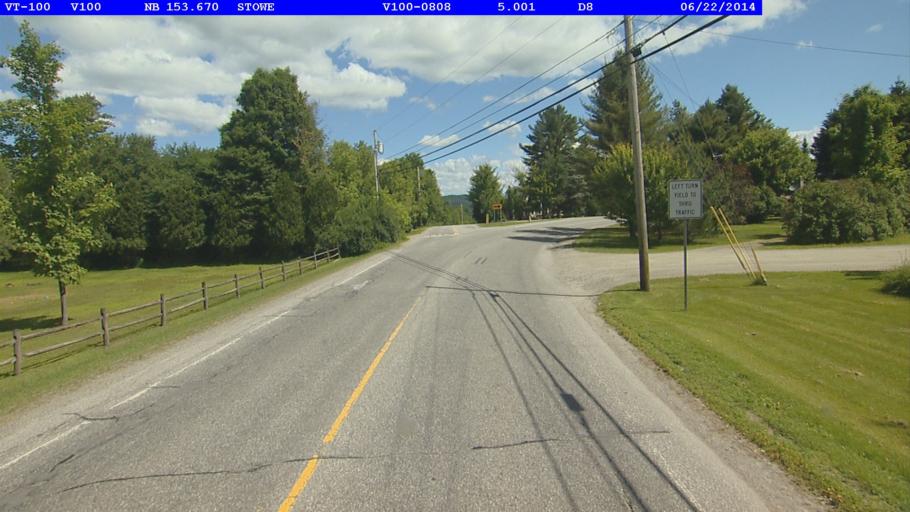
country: US
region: Vermont
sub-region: Lamoille County
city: Morristown
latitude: 44.4814
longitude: -72.6645
